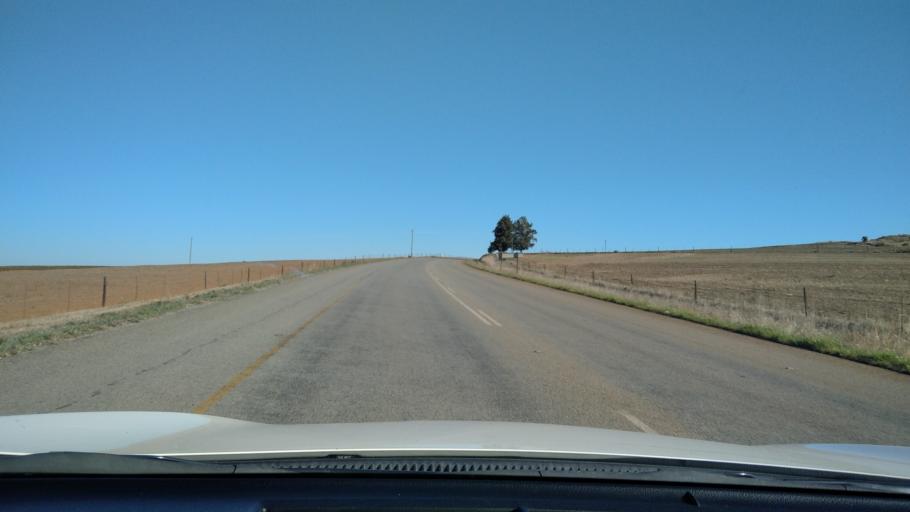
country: ZA
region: Western Cape
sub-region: West Coast District Municipality
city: Malmesbury
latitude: -33.3713
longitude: 18.6543
